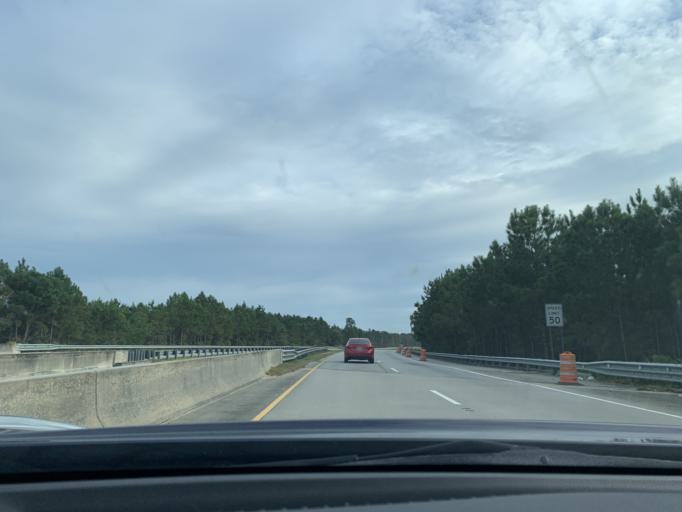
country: US
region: Georgia
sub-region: Chatham County
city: Pooler
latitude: 32.1108
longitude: -81.2669
